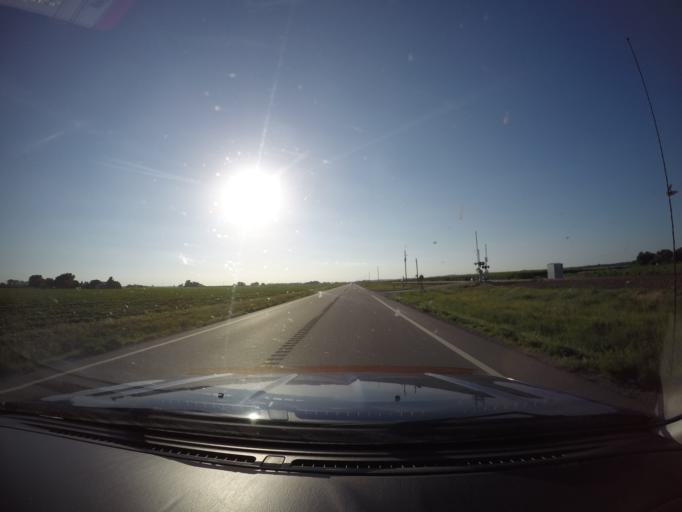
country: US
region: Kansas
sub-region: Shawnee County
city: Rossville
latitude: 39.1459
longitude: -95.9705
